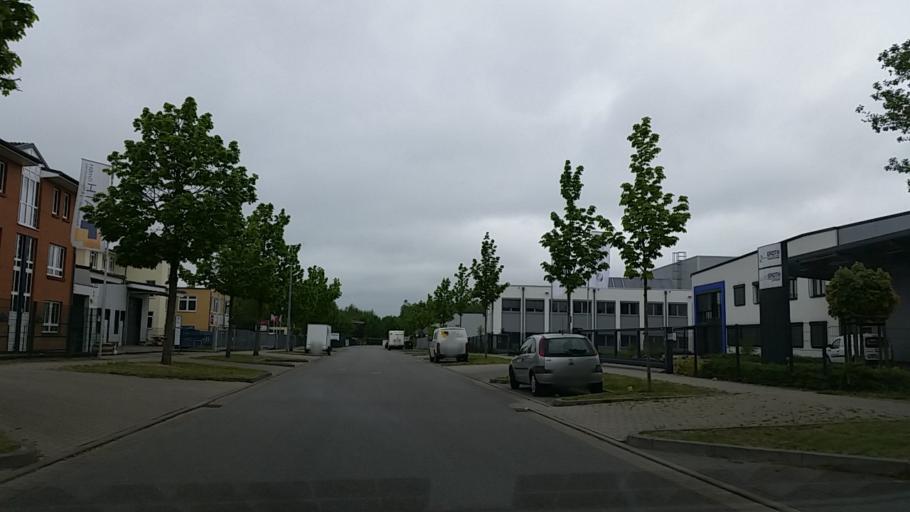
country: DE
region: Schleswig-Holstein
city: Halstenbek
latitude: 53.5939
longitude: 9.8276
